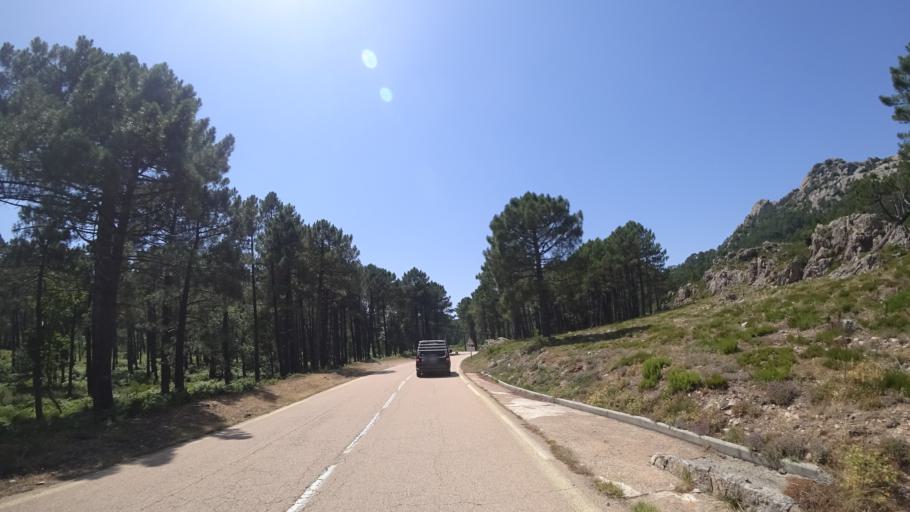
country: FR
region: Corsica
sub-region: Departement de la Corse-du-Sud
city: Zonza
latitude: 41.6872
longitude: 9.1972
